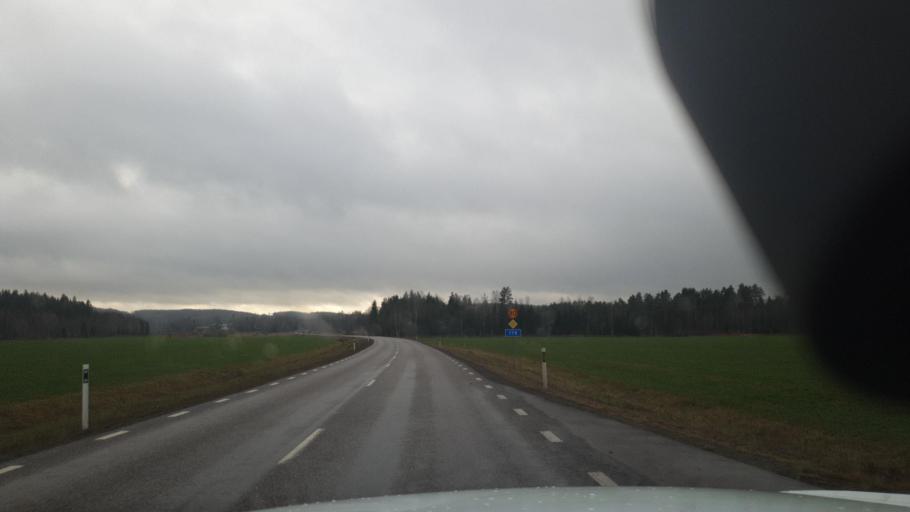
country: SE
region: Vaermland
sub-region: Arvika Kommun
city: Arvika
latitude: 59.4864
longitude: 12.7617
